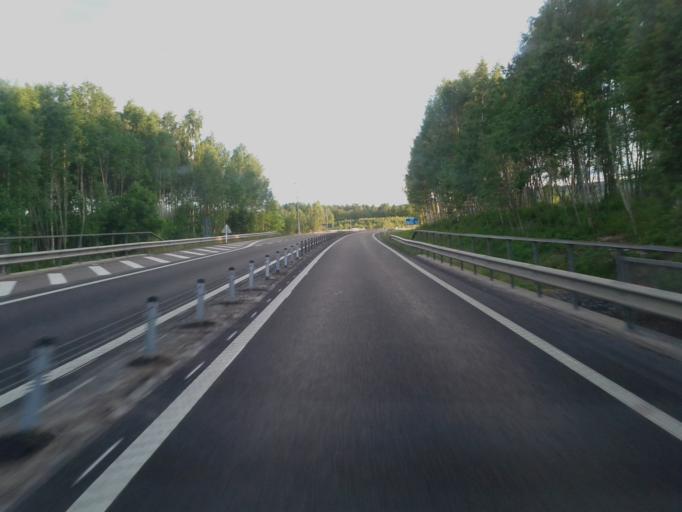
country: SE
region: Dalarna
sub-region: Borlange Kommun
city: Borlaenge
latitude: 60.4661
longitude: 15.3949
